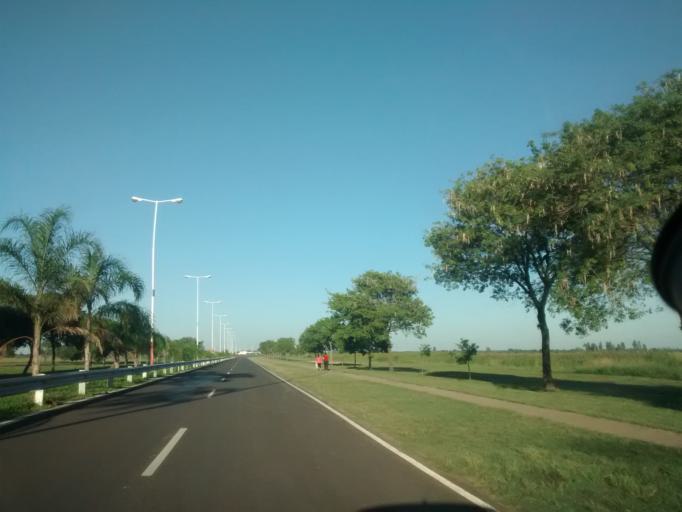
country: AR
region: Chaco
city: Fontana
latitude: -27.4415
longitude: -59.0358
